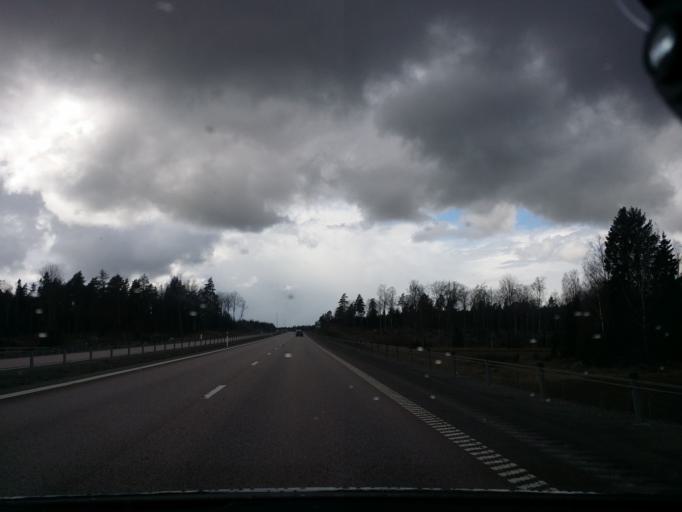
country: SE
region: Uppsala
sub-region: Enkopings Kommun
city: Hummelsta
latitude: 59.6394
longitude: 16.9305
